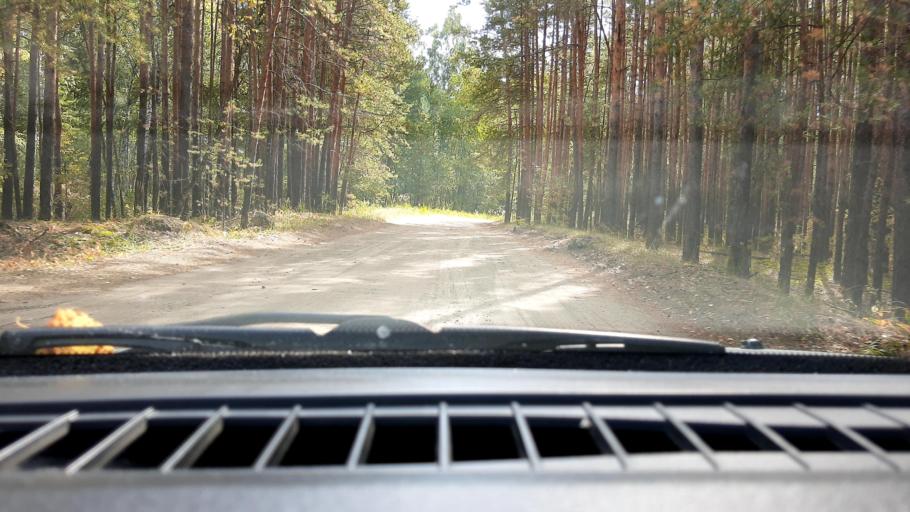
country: RU
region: Nizjnij Novgorod
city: Gorbatovka
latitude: 56.3158
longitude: 43.6955
